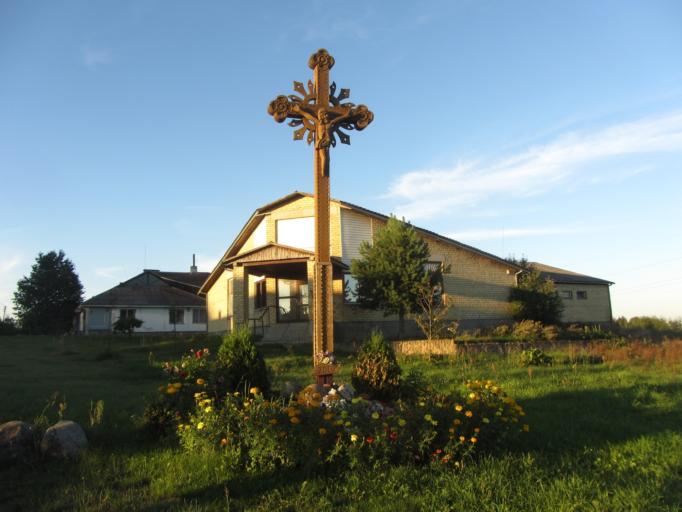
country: LT
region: Alytaus apskritis
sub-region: Alytus
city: Alytus
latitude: 54.3623
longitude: 23.9850
